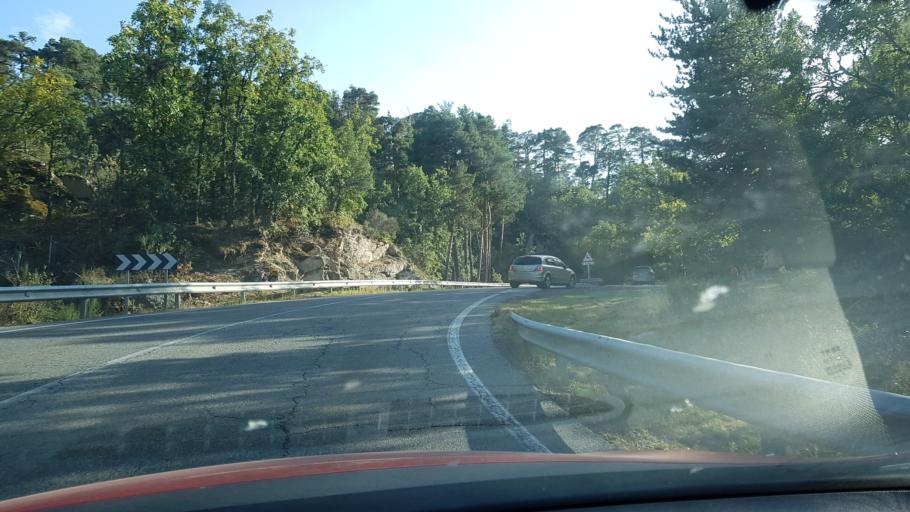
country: ES
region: Castille and Leon
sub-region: Provincia de Segovia
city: San Ildefonso
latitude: 40.8551
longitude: -4.0263
